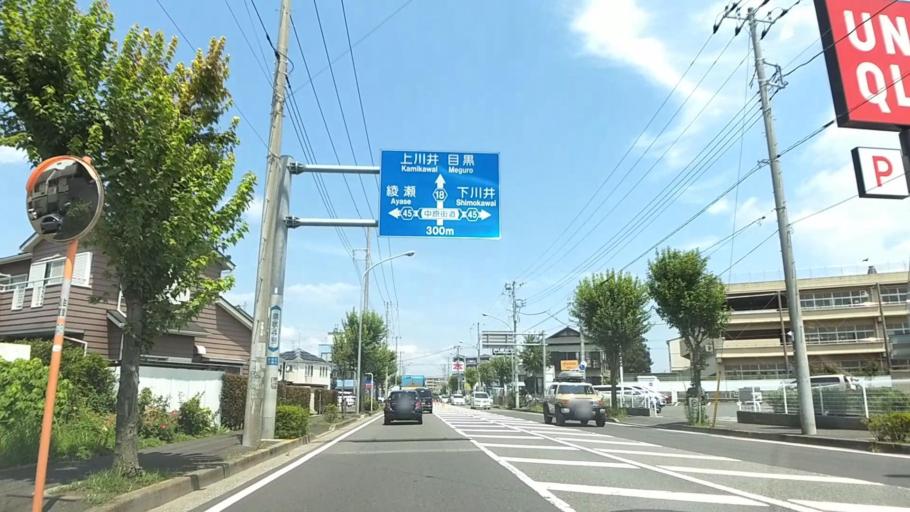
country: JP
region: Kanagawa
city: Minami-rinkan
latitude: 35.4559
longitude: 139.4816
